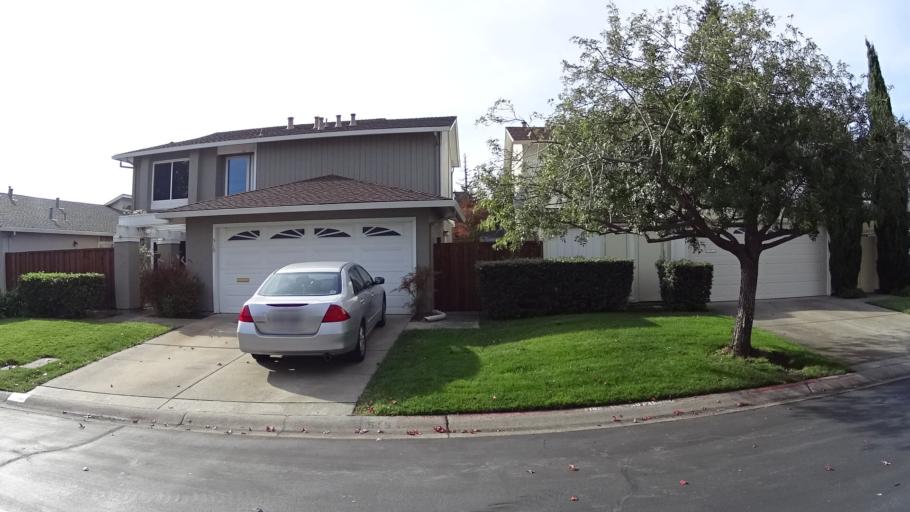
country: US
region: California
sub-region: San Mateo County
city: Foster City
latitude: 37.5402
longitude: -122.2686
